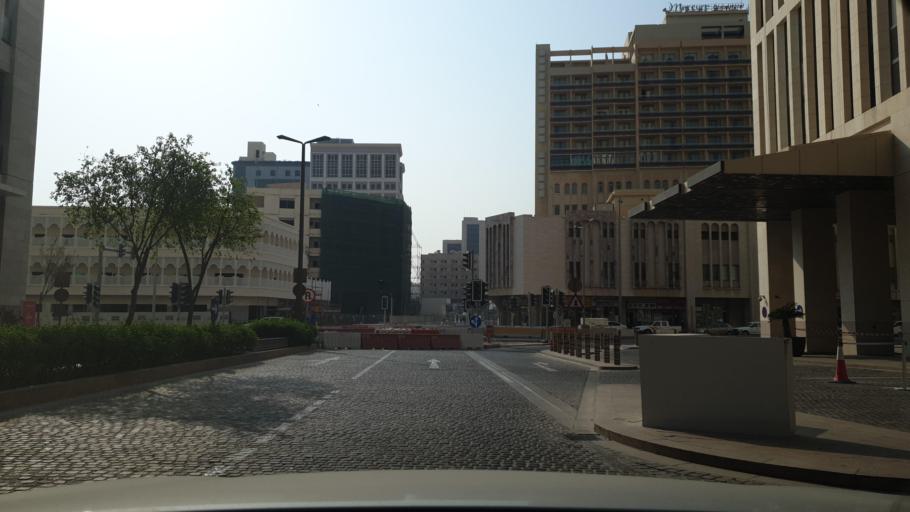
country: QA
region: Baladiyat ad Dawhah
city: Doha
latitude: 25.2846
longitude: 51.5281
